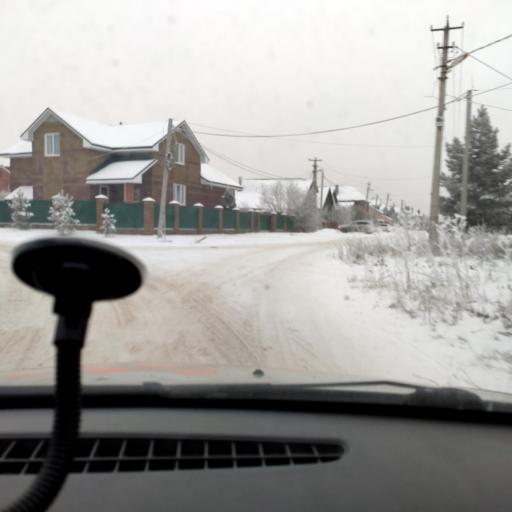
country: RU
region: Bashkortostan
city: Ufa
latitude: 54.6012
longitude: 55.9322
